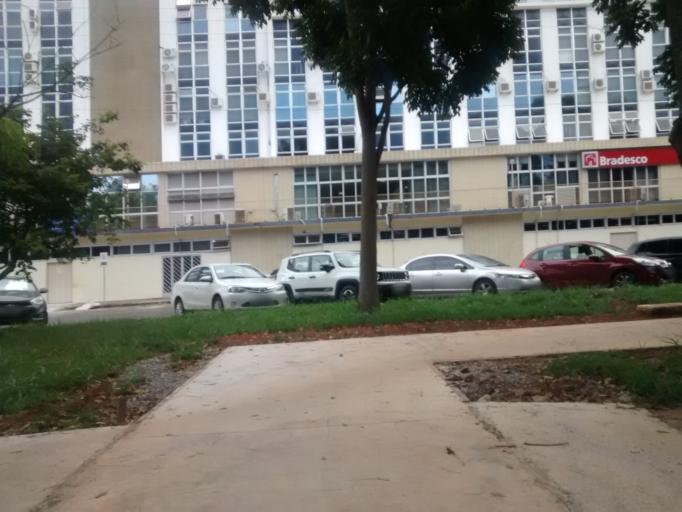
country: BR
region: Federal District
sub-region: Brasilia
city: Brasilia
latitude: -15.7479
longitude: -47.8952
